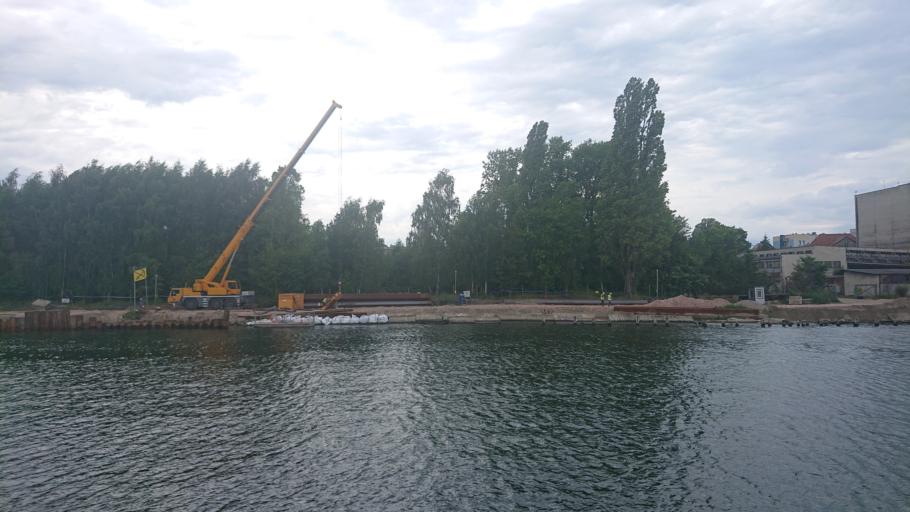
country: PL
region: Pomeranian Voivodeship
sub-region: Gdansk
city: Gdansk
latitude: 54.3982
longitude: 18.6794
